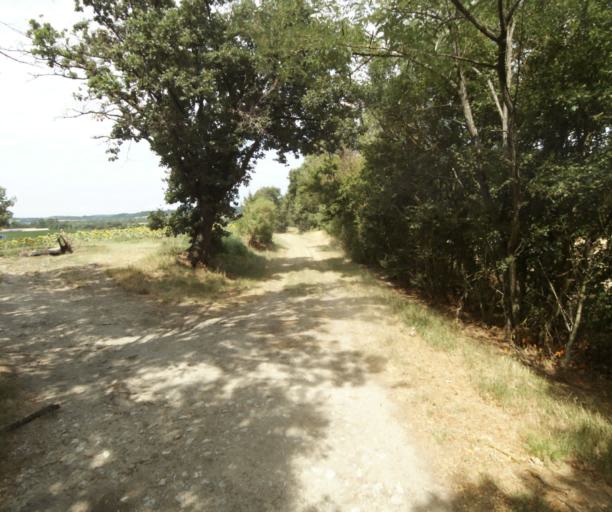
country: FR
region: Midi-Pyrenees
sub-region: Departement de la Haute-Garonne
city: Saint-Felix-Lauragais
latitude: 43.4297
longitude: 1.9186
